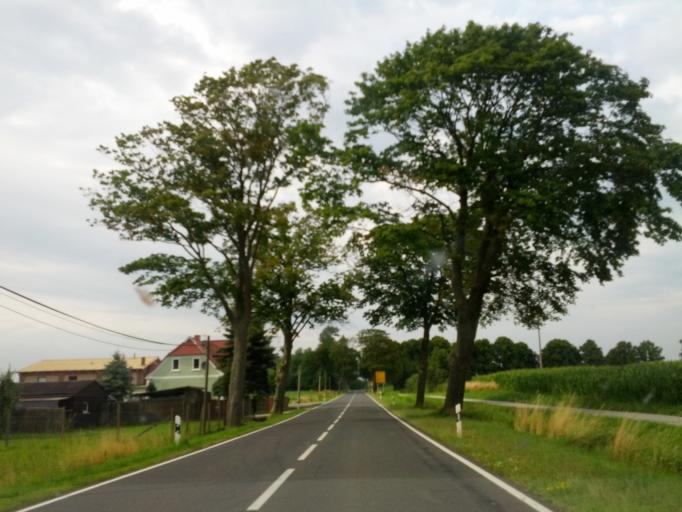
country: DE
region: Mecklenburg-Vorpommern
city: Kropelin
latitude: 54.0555
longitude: 11.7997
